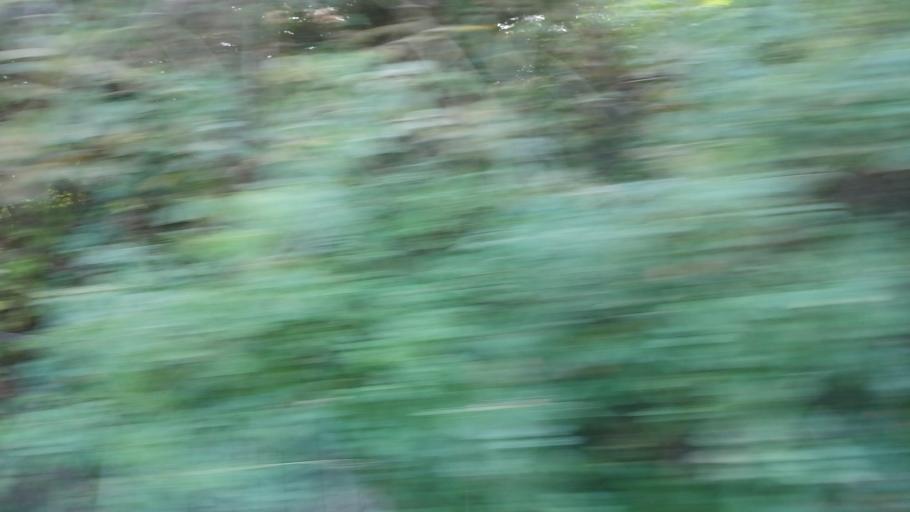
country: CY
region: Pafos
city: Pegeia
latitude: 34.9364
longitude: 32.4595
